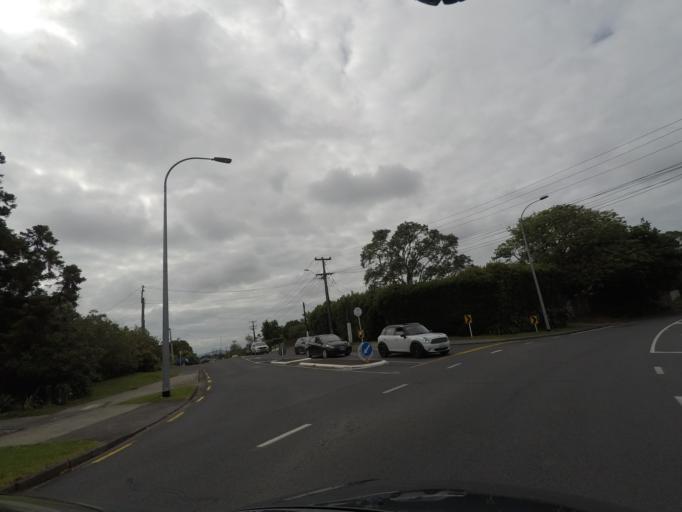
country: NZ
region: Auckland
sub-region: Auckland
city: Rosebank
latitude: -36.8443
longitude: 174.6079
